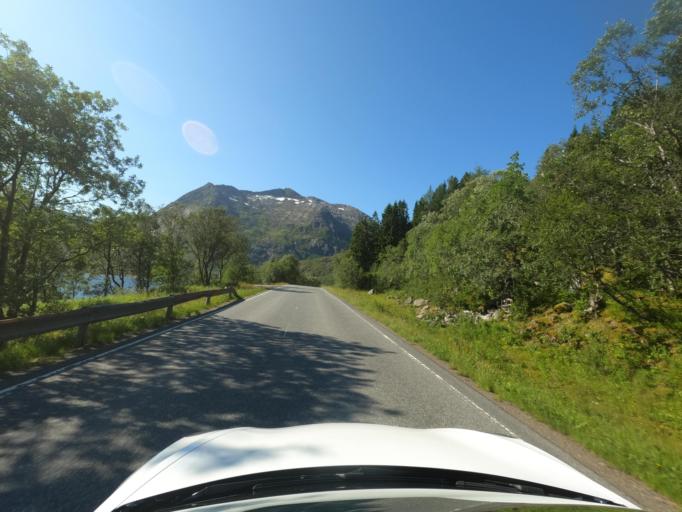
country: NO
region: Nordland
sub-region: Lodingen
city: Lodingen
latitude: 68.5427
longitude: 15.7316
